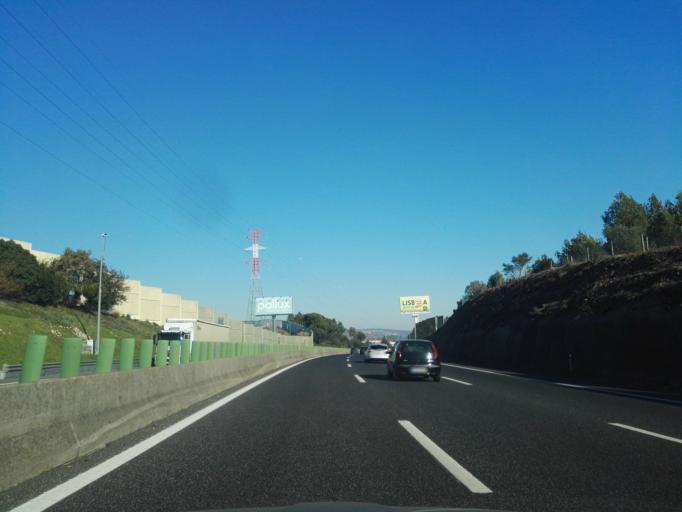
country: PT
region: Lisbon
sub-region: Vila Franca de Xira
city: Vialonga
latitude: 38.8627
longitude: -9.0808
